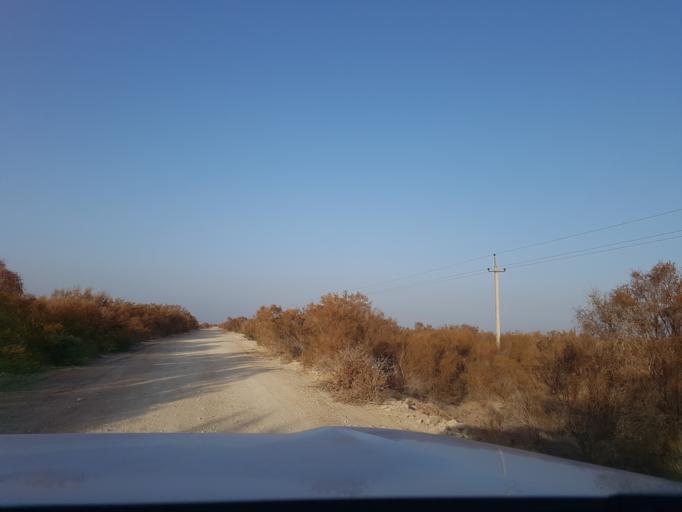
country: TM
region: Dasoguz
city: Koeneuergench
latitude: 41.8532
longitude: 58.2527
